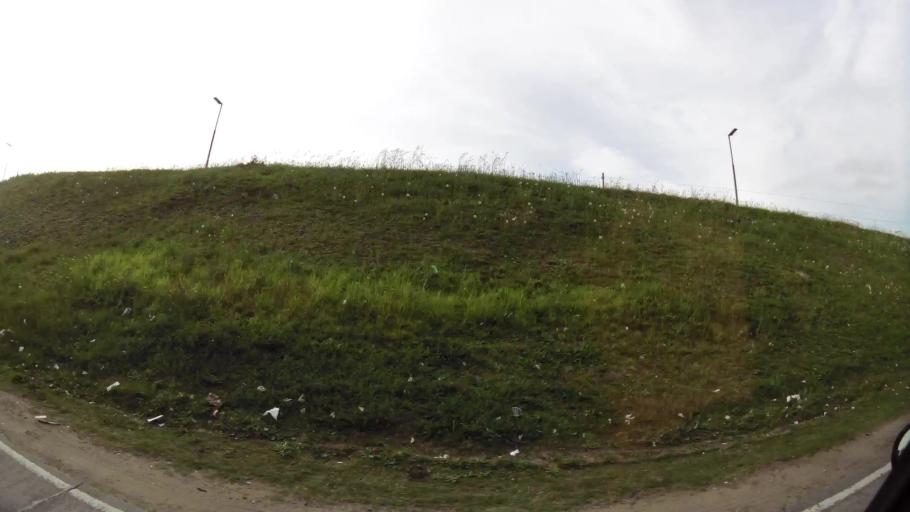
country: AR
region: Buenos Aires
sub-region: Partido de Quilmes
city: Quilmes
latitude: -34.7022
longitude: -58.2749
